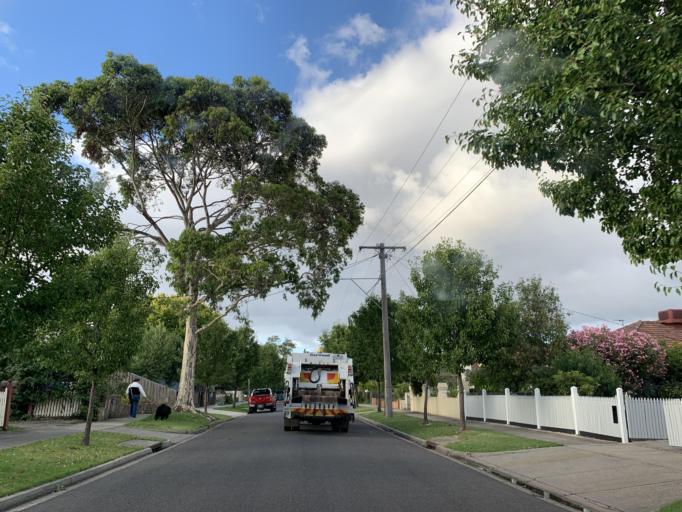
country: AU
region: Victoria
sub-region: Moonee Valley
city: Niddrie
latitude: -37.7375
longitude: 144.8987
